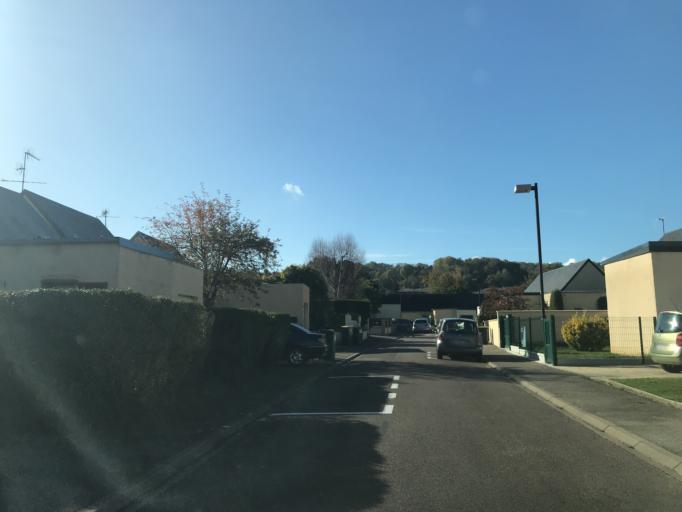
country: FR
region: Haute-Normandie
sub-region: Departement de l'Eure
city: Saint-Marcel
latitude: 49.1027
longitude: 1.4485
